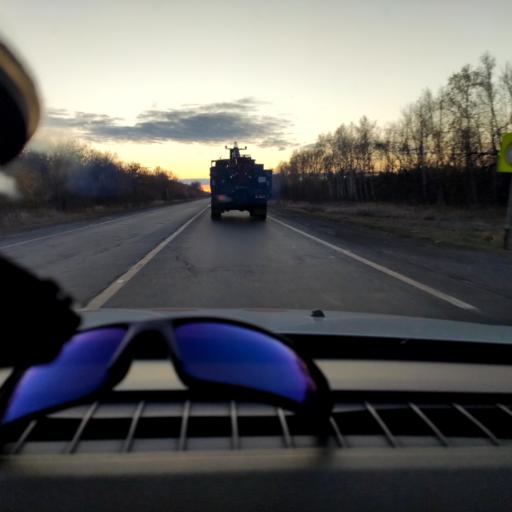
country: RU
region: Samara
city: Chapayevsk
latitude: 52.9900
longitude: 49.8469
